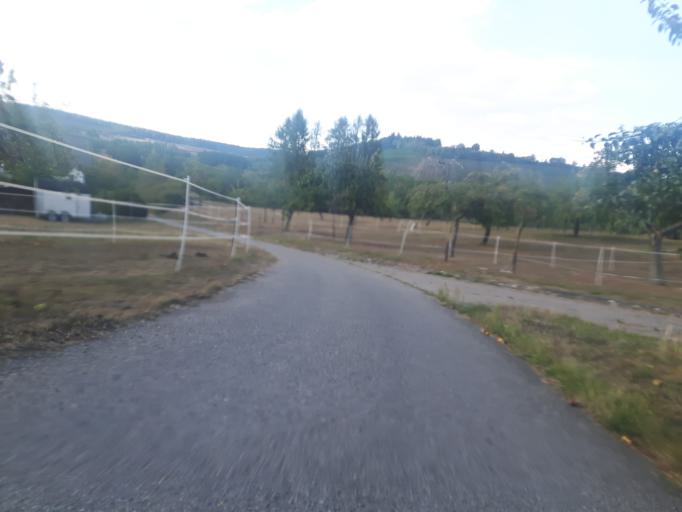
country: DE
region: Baden-Wuerttemberg
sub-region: Regierungsbezirk Stuttgart
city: Zaberfeld
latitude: 49.0545
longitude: 8.9417
